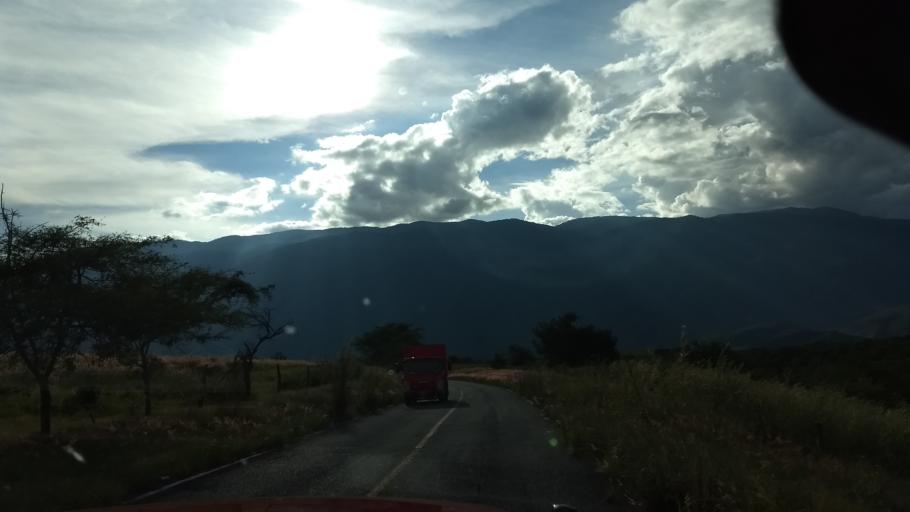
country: MX
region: Colima
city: Suchitlan
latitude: 19.4555
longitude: -103.8035
